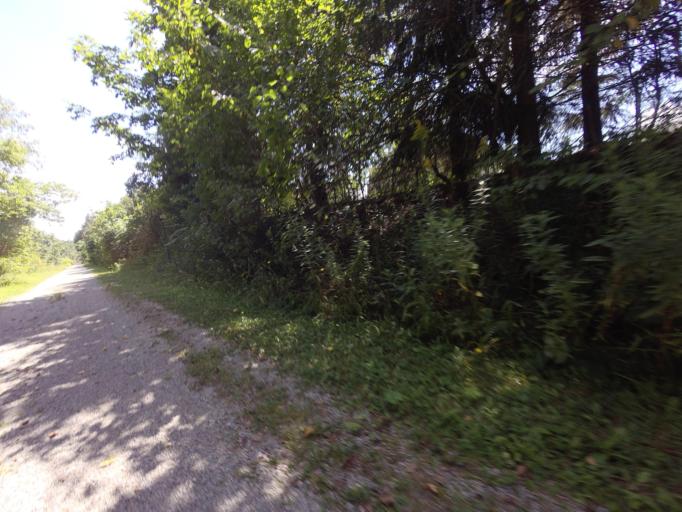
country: CA
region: Ontario
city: Orangeville
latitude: 43.7833
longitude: -80.1322
